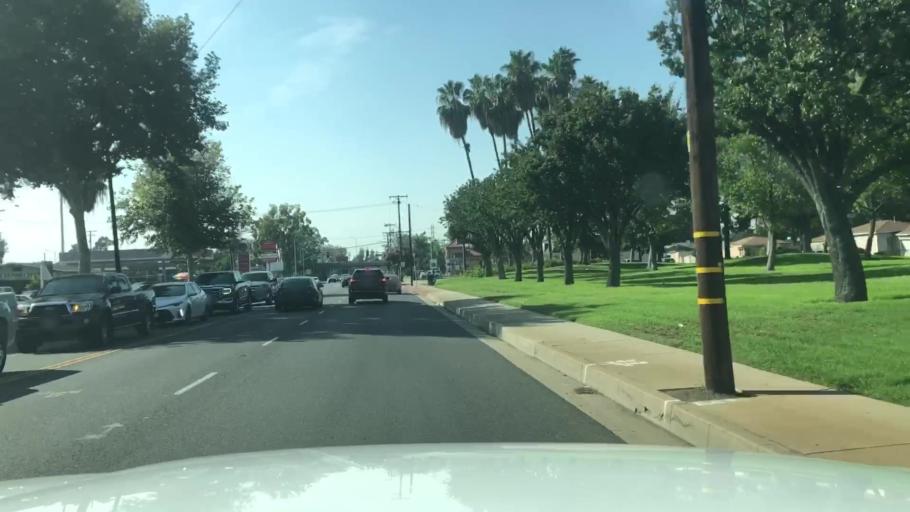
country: US
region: California
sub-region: Los Angeles County
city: West Whittier-Los Nietos
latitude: 33.9914
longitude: -118.0660
